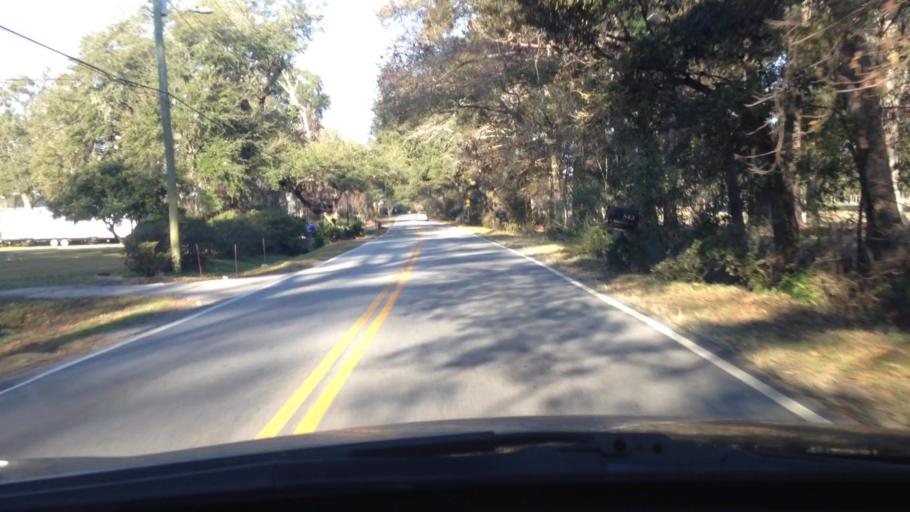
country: US
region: South Carolina
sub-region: Charleston County
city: Charleston
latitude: 32.7509
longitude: -79.9912
